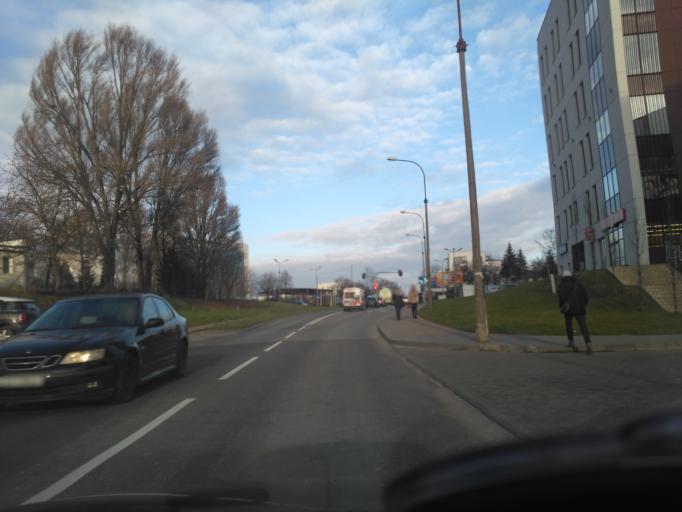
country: PL
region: Lublin Voivodeship
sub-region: Powiat lubelski
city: Lublin
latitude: 51.2624
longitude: 22.5635
